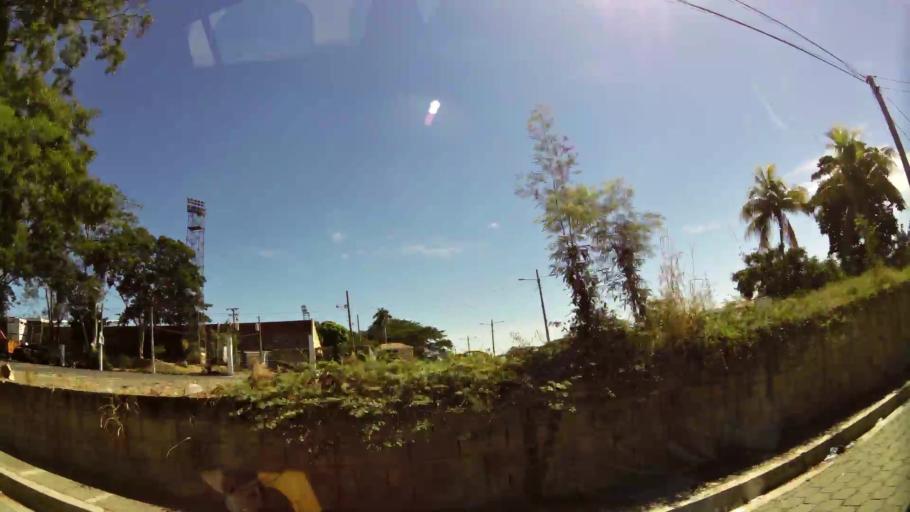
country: SV
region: San Miguel
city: San Miguel
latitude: 13.4821
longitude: -88.1704
